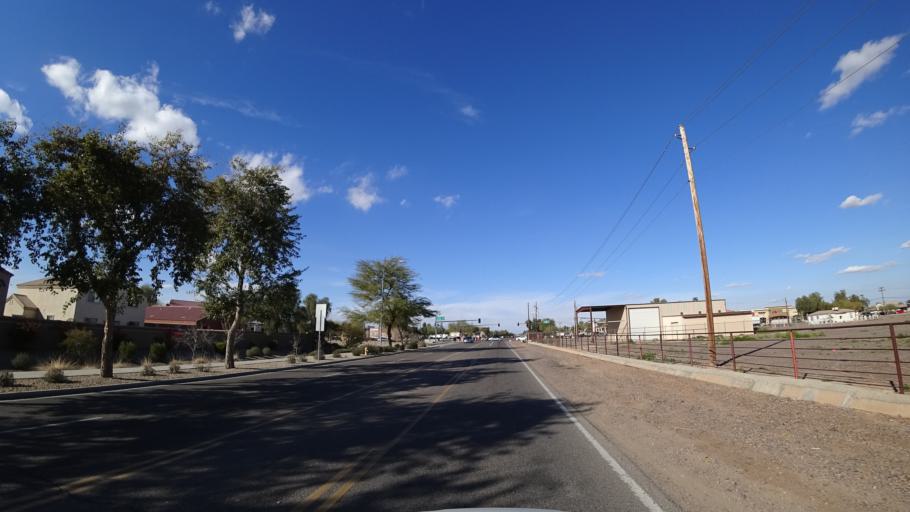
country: US
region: Arizona
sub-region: Maricopa County
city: Tolleson
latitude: 33.4216
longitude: -112.2386
